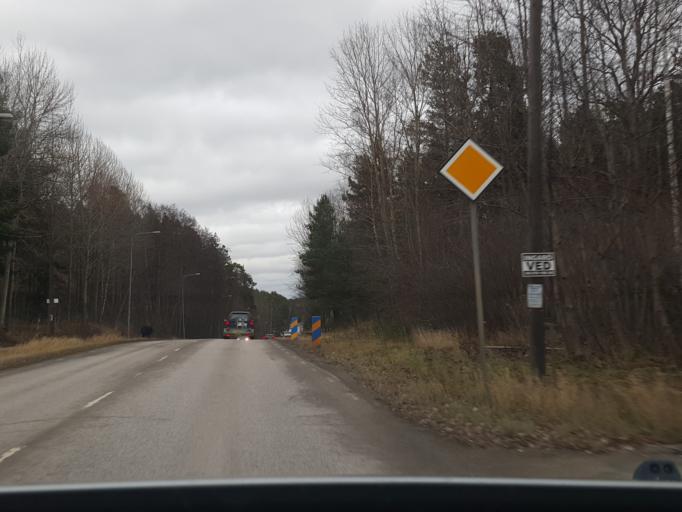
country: SE
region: Stockholm
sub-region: Nacka Kommun
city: Boo
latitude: 59.3232
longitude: 18.2602
